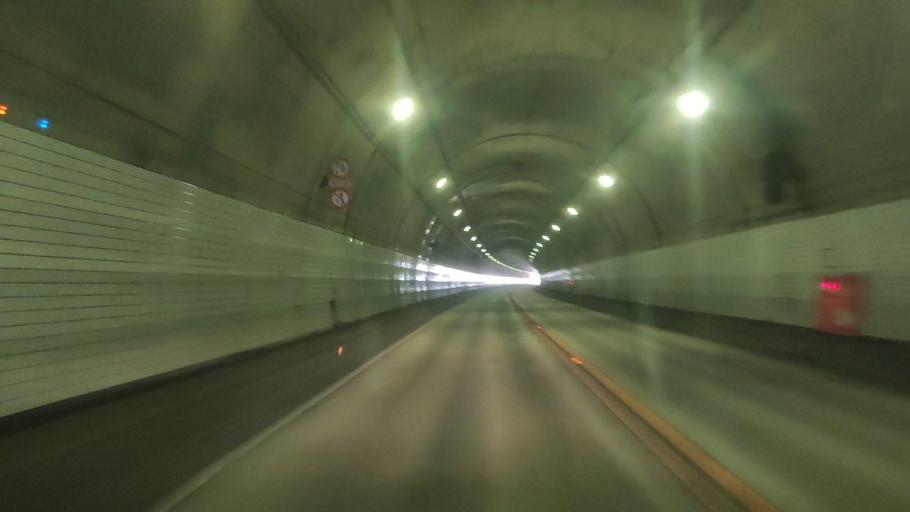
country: JP
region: Fukuoka
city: Maebaru-chuo
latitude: 33.4676
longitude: 130.2800
